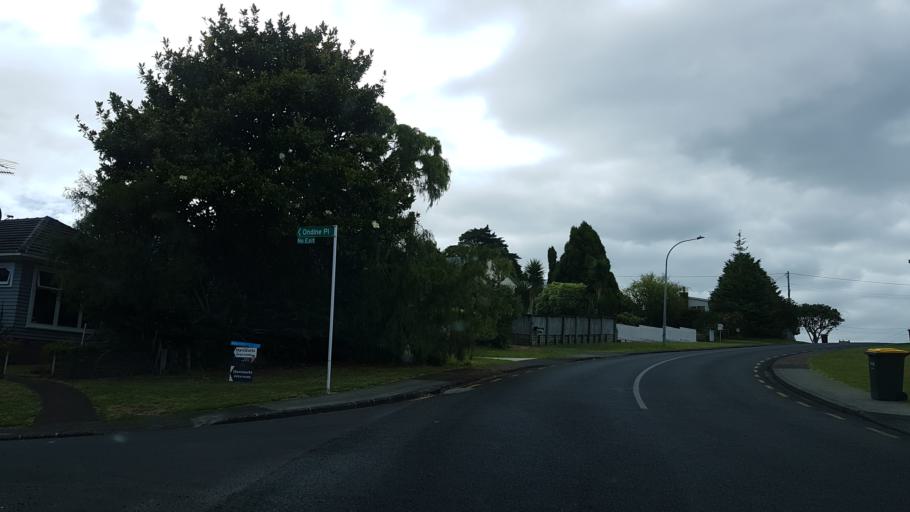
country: NZ
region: Auckland
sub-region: Auckland
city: North Shore
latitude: -36.7750
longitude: 174.7253
